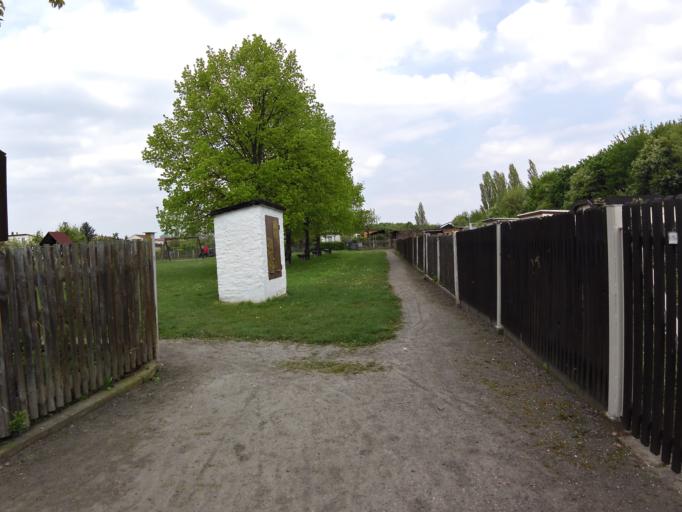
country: DE
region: Saxony
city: Leipzig
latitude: 51.3711
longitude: 12.3925
